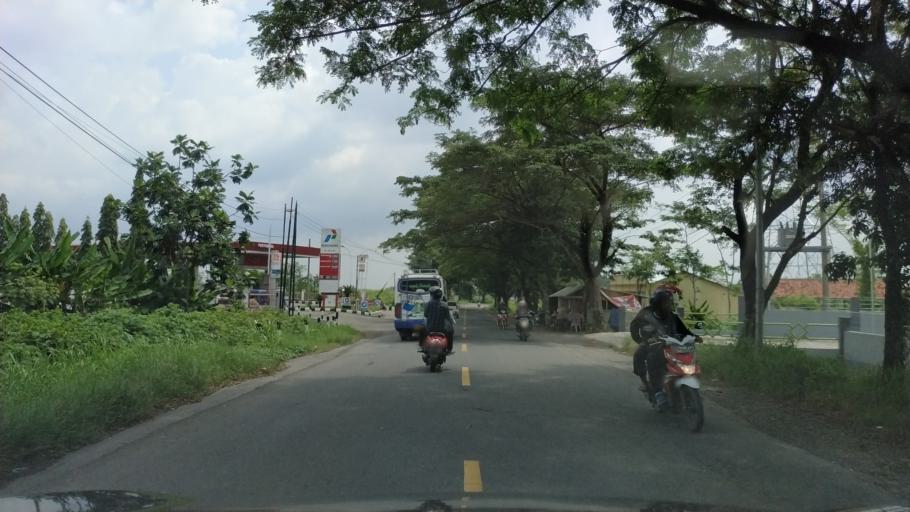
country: ID
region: Central Java
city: Lebaksiu
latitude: -7.0312
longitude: 109.1440
